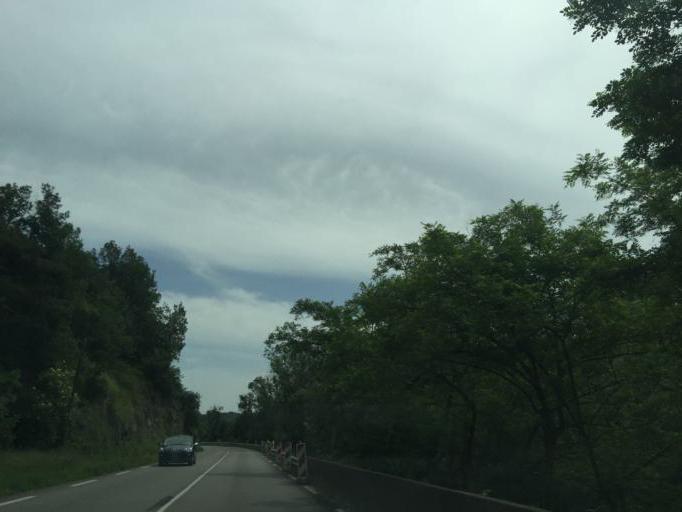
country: FR
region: Rhone-Alpes
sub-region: Departement de l'Ardeche
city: Saint-Marcel-les-Annonay
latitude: 45.2897
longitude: 4.5967
